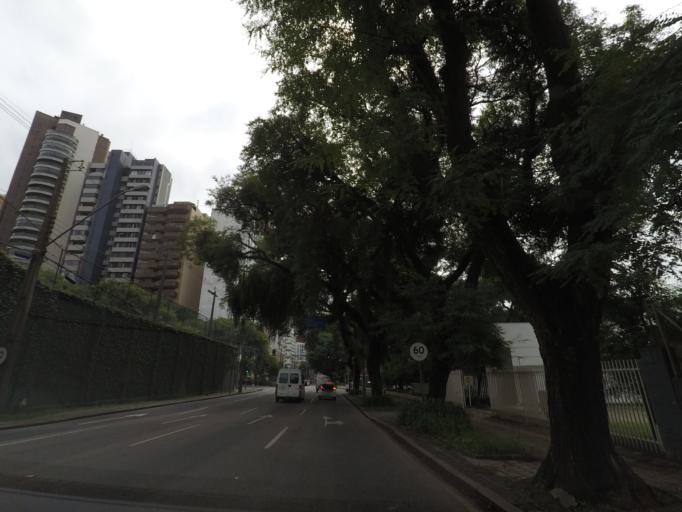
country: BR
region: Parana
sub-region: Curitiba
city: Curitiba
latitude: -25.4508
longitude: -49.2851
